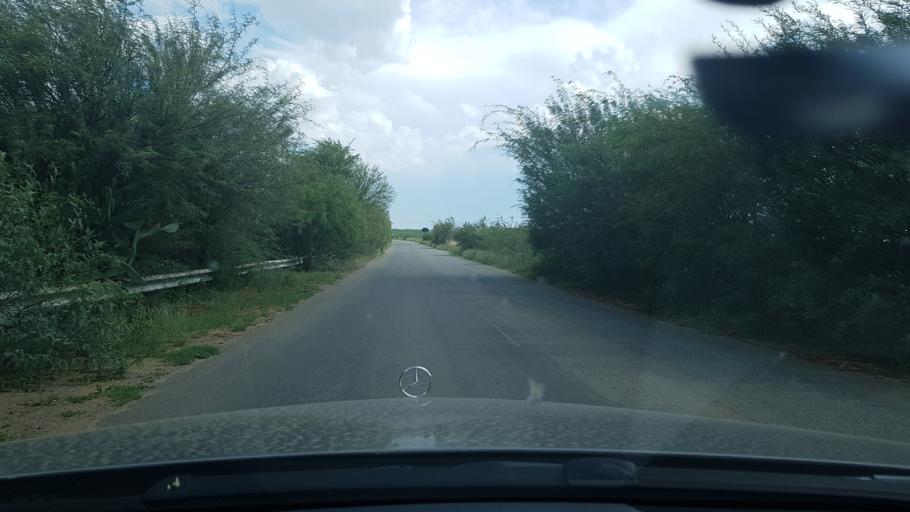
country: ZA
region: North-West
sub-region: Dr Ruth Segomotsi Mompati District Municipality
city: Bloemhof
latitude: -27.6572
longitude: 25.5945
